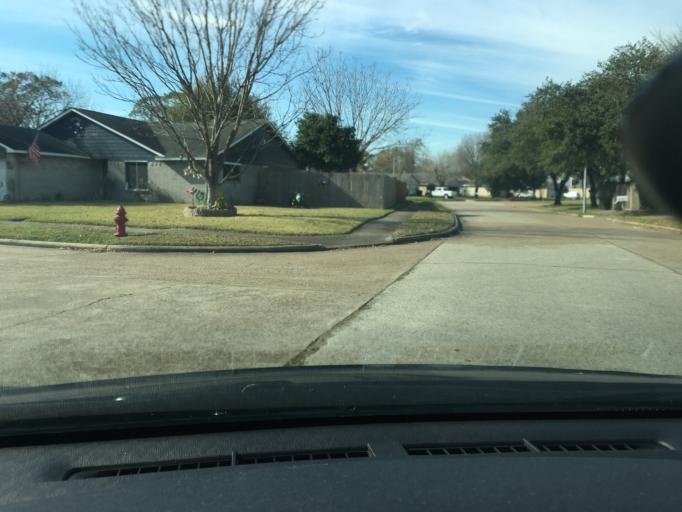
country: US
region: Texas
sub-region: Harris County
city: Cloverleaf
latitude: 29.8083
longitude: -95.1585
